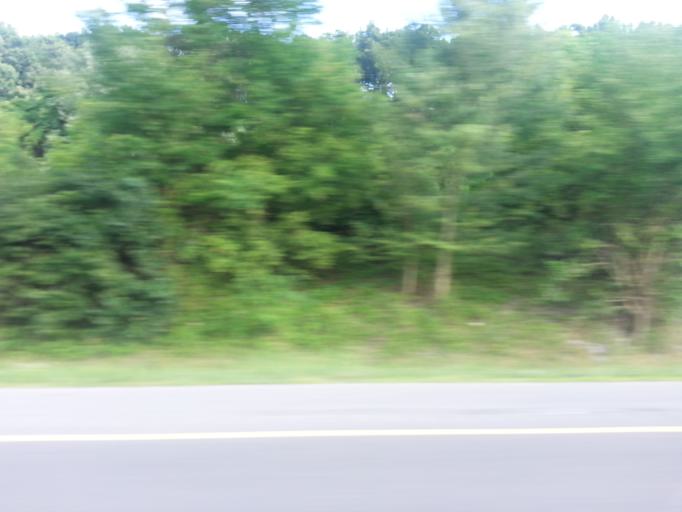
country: US
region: Tennessee
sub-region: Knox County
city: Knoxville
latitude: 36.0280
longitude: -83.9009
